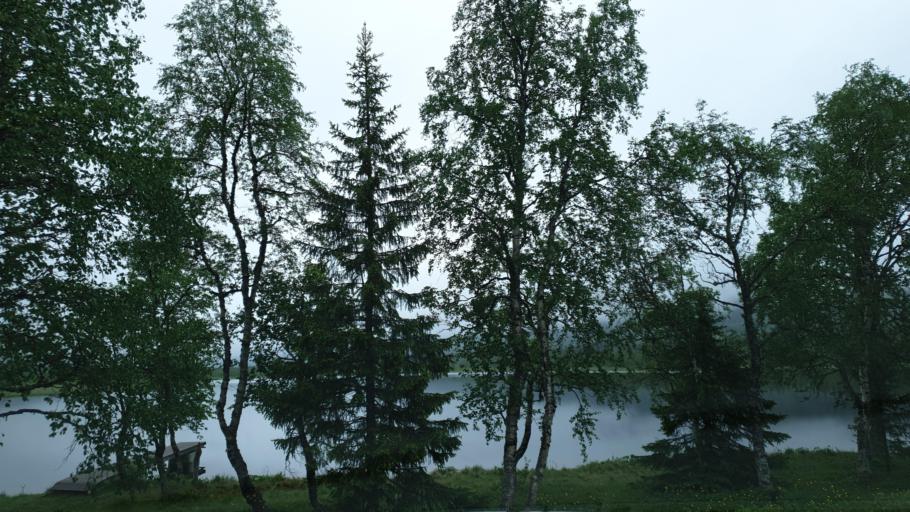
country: SE
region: Vaesterbotten
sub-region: Vilhelmina Kommun
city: Sjoberg
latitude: 65.3355
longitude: 15.8724
